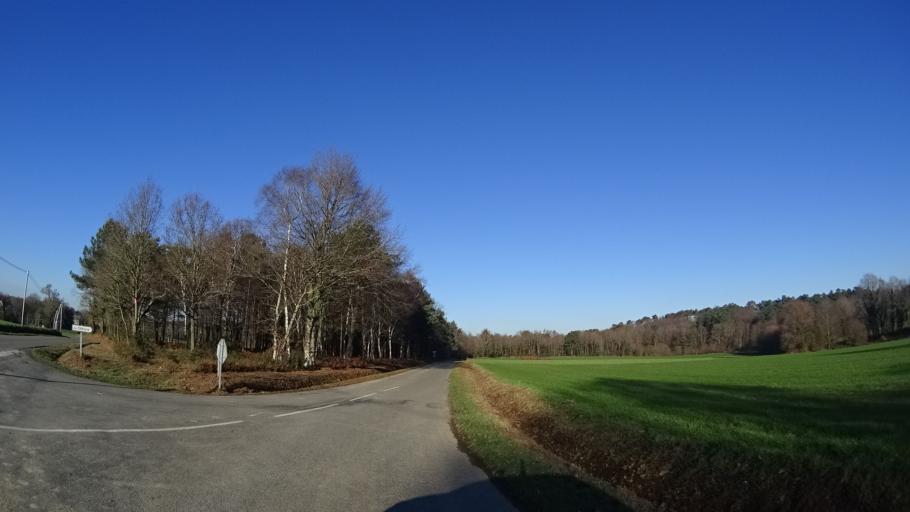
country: FR
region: Brittany
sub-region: Departement du Morbihan
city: Allaire
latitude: 47.6470
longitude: -2.1790
